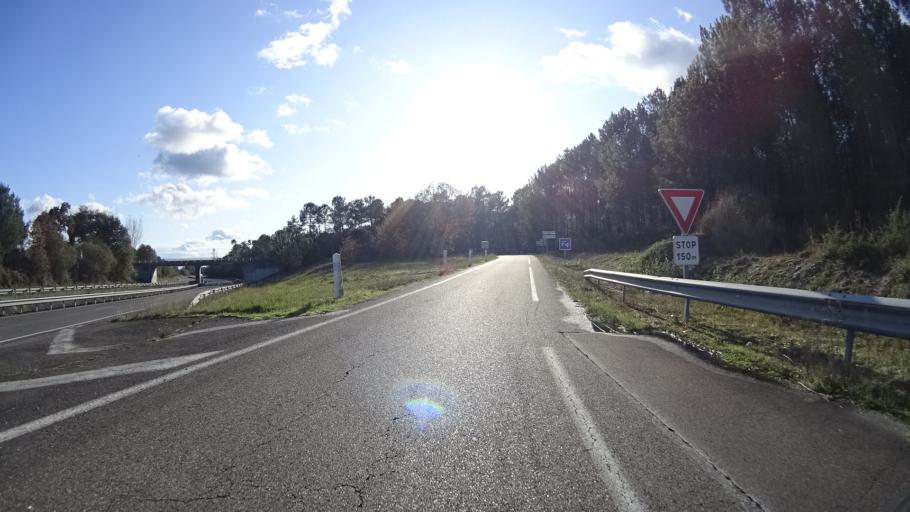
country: FR
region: Aquitaine
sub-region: Departement des Landes
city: Mees
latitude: 43.7337
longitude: -1.1024
